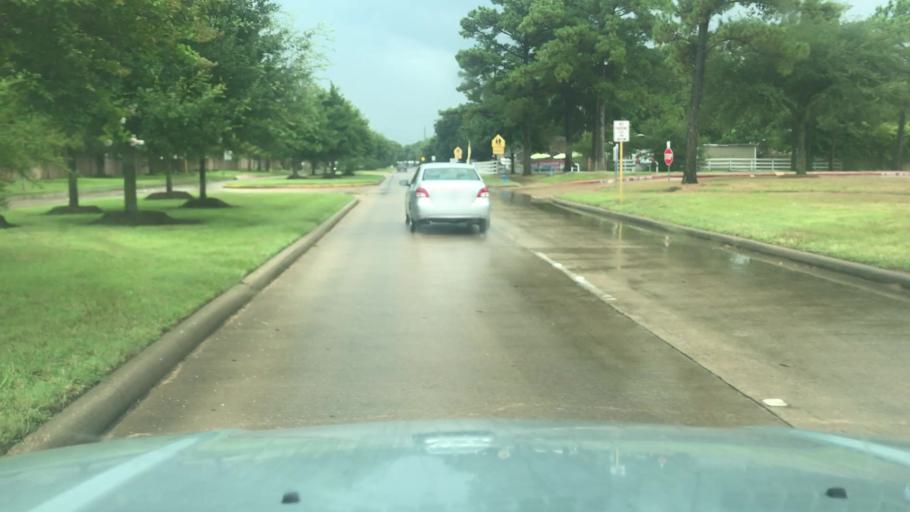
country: US
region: Texas
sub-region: Fort Bend County
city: Cinco Ranch
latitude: 29.7432
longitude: -95.7903
